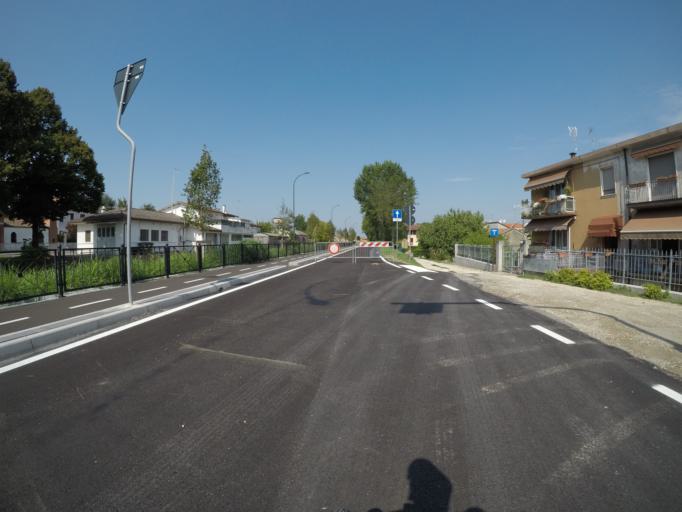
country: IT
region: Veneto
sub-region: Provincia di Rovigo
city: Lendinara
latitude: 45.0846
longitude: 11.5929
